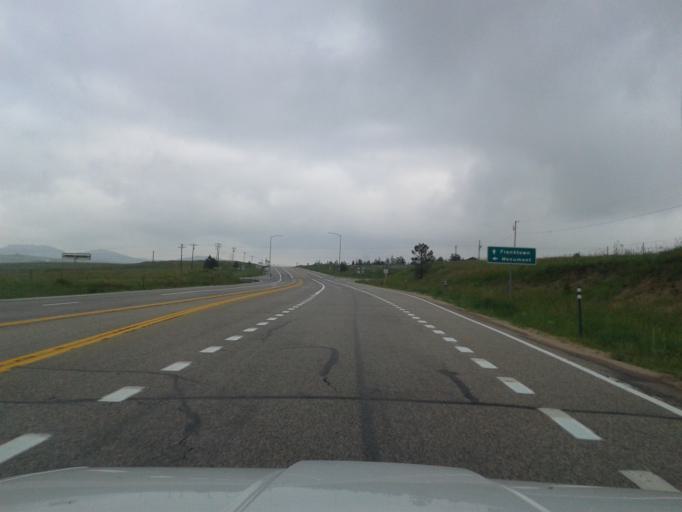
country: US
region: Colorado
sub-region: El Paso County
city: Gleneagle
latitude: 39.0983
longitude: -104.7706
